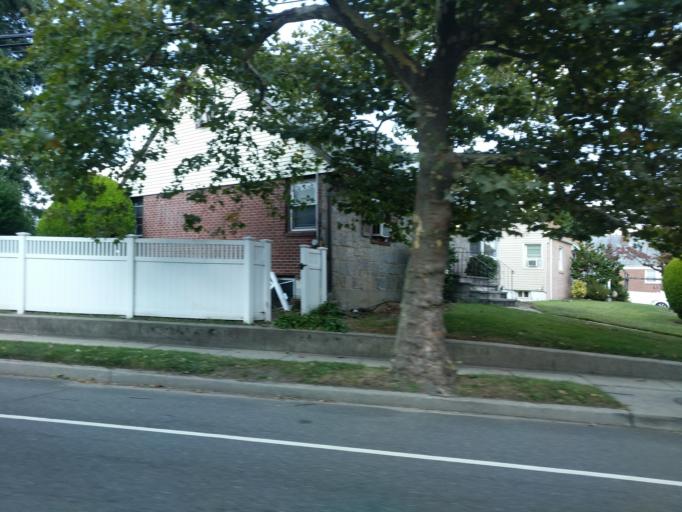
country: US
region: New York
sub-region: Nassau County
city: Hewlett
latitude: 40.6480
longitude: -73.7070
